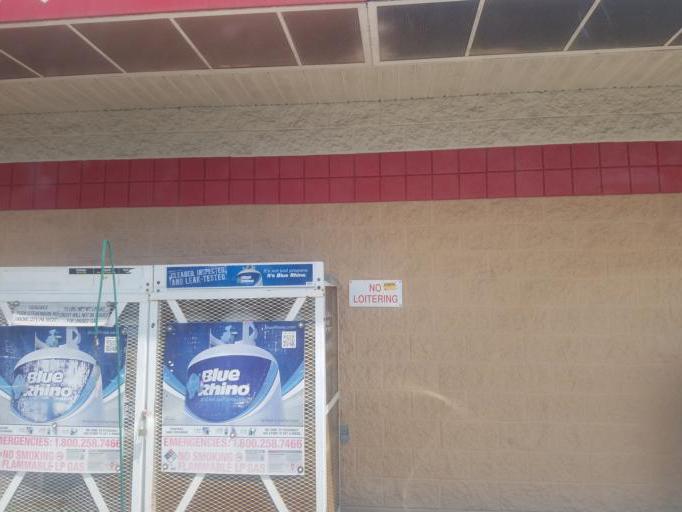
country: US
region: Ohio
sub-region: Muskingum County
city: Zanesville
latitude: 39.9496
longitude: -82.0479
